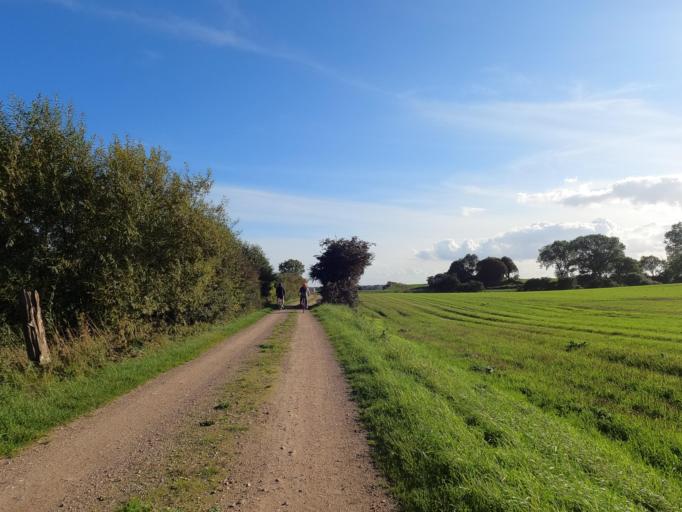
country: DE
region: Schleswig-Holstein
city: Neukirchen
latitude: 54.3486
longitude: 11.0448
